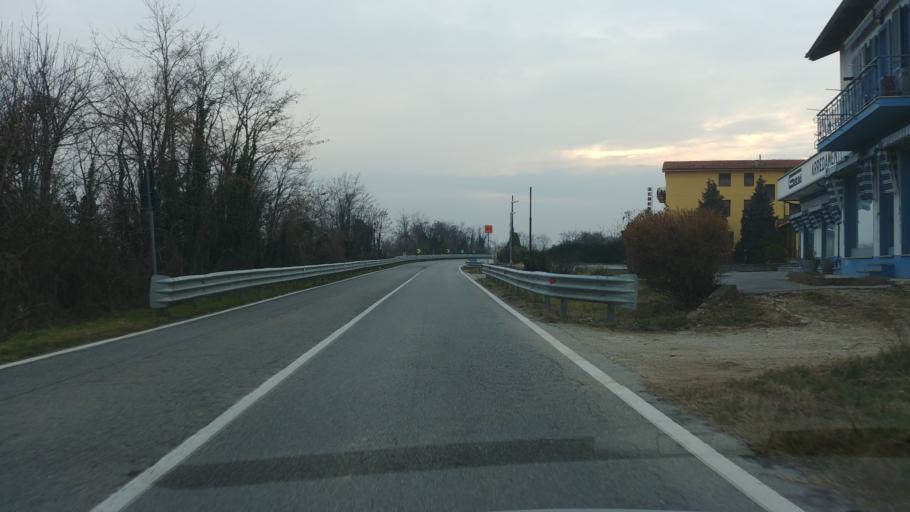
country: IT
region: Piedmont
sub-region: Provincia di Cuneo
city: Castelletto Stura
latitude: 44.4504
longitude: 7.6195
